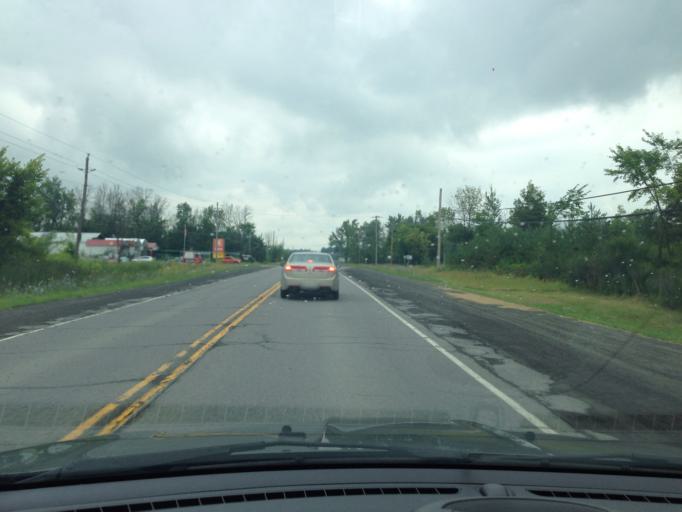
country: CA
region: Ontario
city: Ottawa
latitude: 45.3084
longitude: -75.5867
